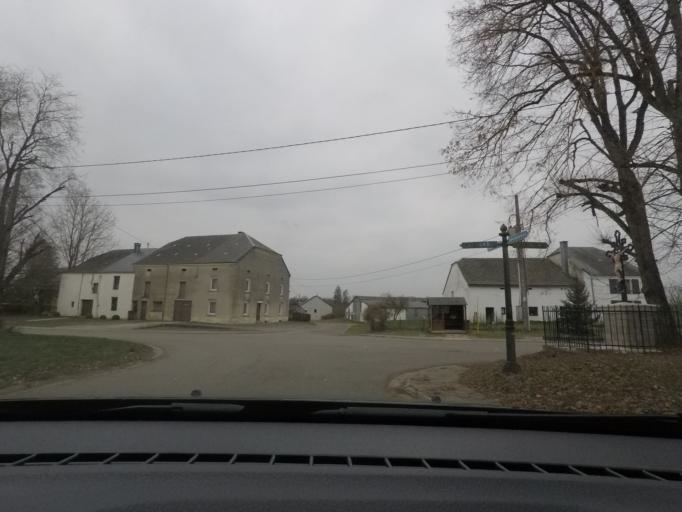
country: BE
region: Wallonia
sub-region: Province du Luxembourg
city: Etalle
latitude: 49.7062
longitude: 5.5866
